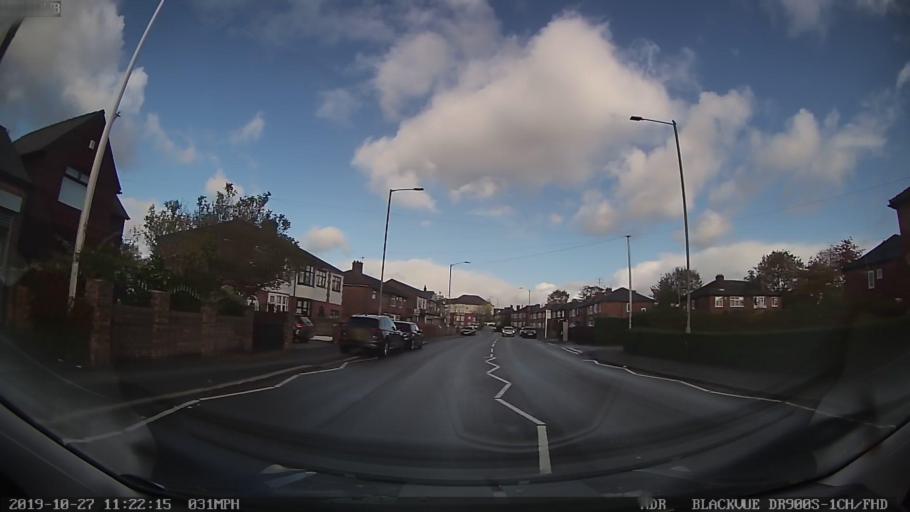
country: GB
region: England
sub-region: Manchester
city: Failsworth
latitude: 53.5211
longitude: -2.1822
